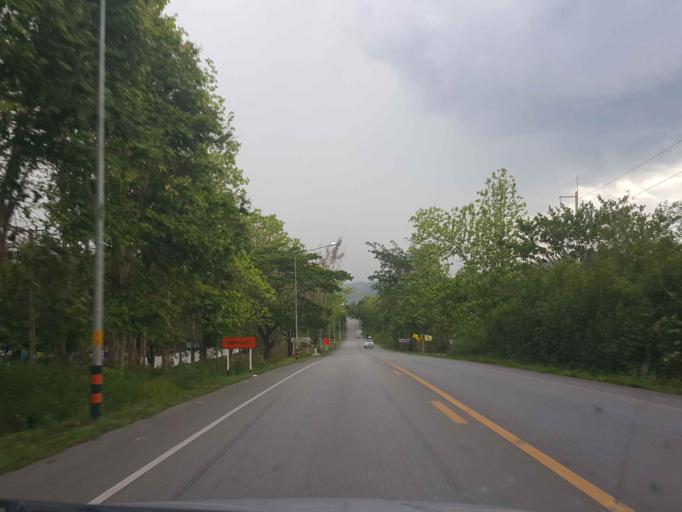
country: TH
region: Phrae
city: Den Chai
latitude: 17.9734
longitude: 100.0422
